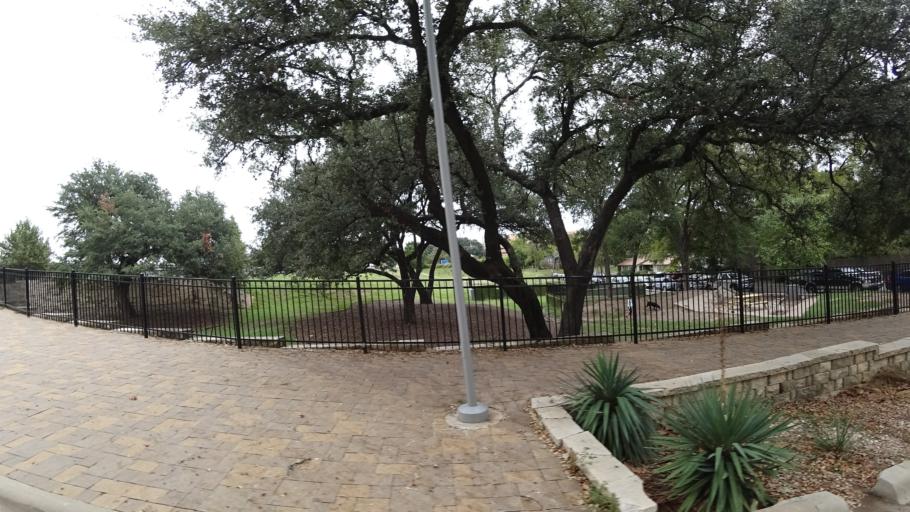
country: US
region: Texas
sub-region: Travis County
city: Austin
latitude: 30.2916
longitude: -97.7238
